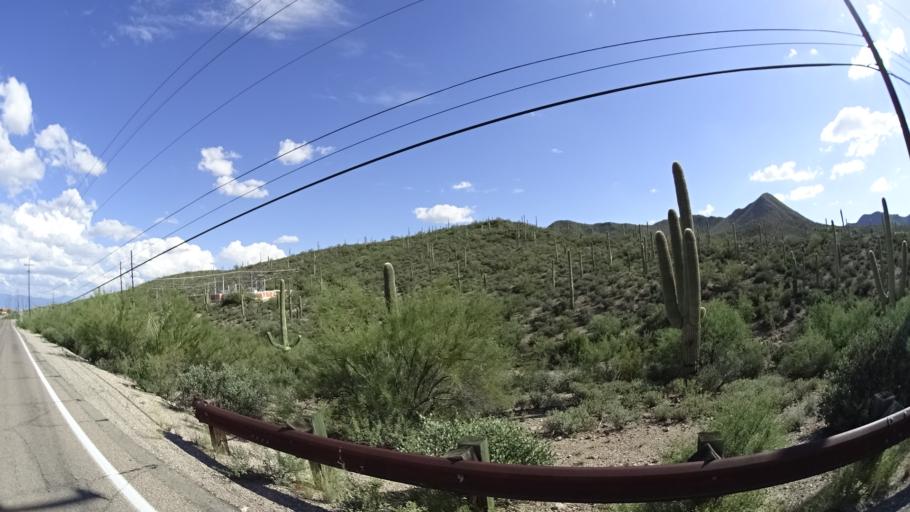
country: US
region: Arizona
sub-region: Pima County
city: Tucson Estates
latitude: 32.2392
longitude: -111.0494
